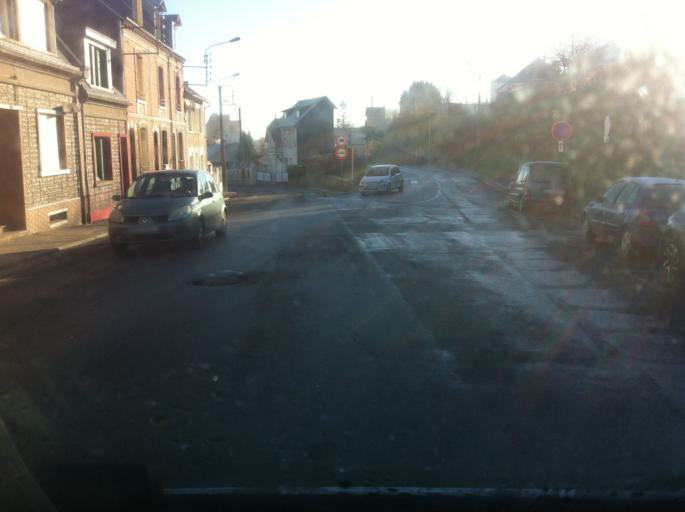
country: FR
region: Haute-Normandie
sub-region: Departement de la Seine-Maritime
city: Le Treport
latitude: 50.0577
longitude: 1.3789
